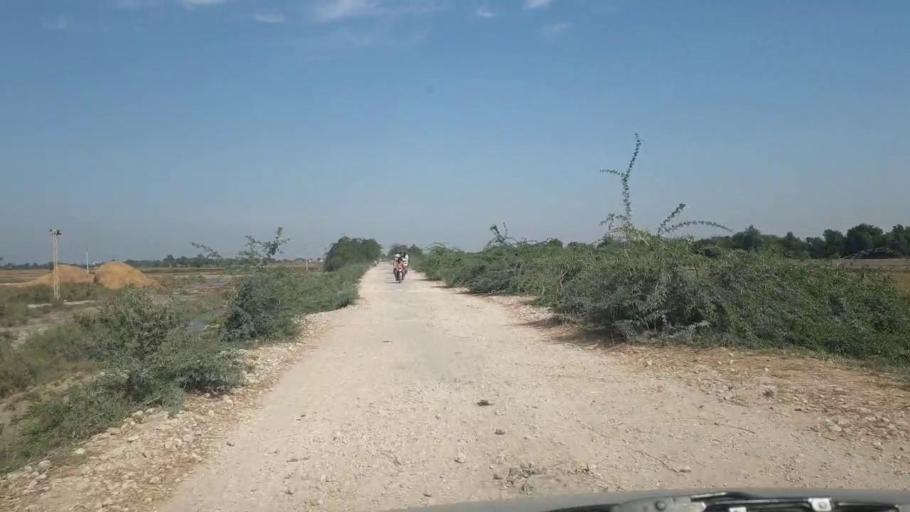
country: PK
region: Sindh
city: Tando Bago
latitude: 24.8816
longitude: 69.0009
